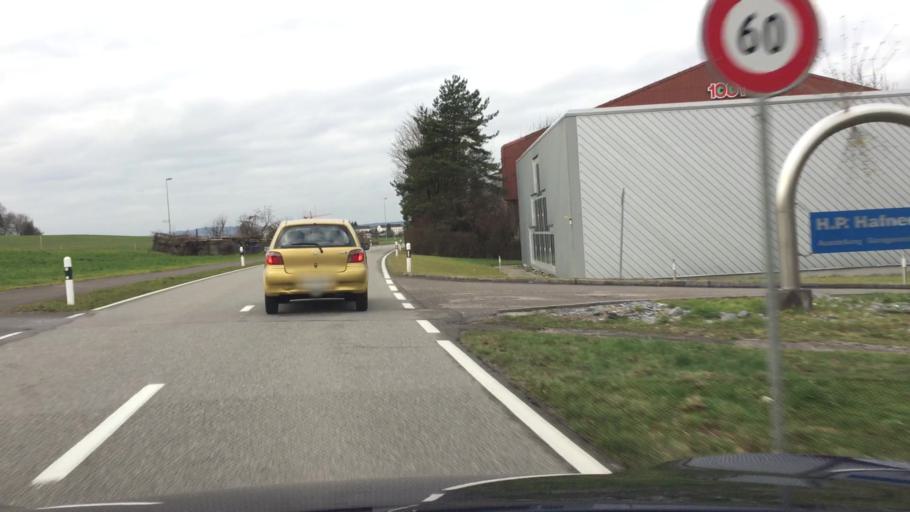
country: CH
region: Thurgau
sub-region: Arbon District
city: Amriswil
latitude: 47.5403
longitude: 9.2905
